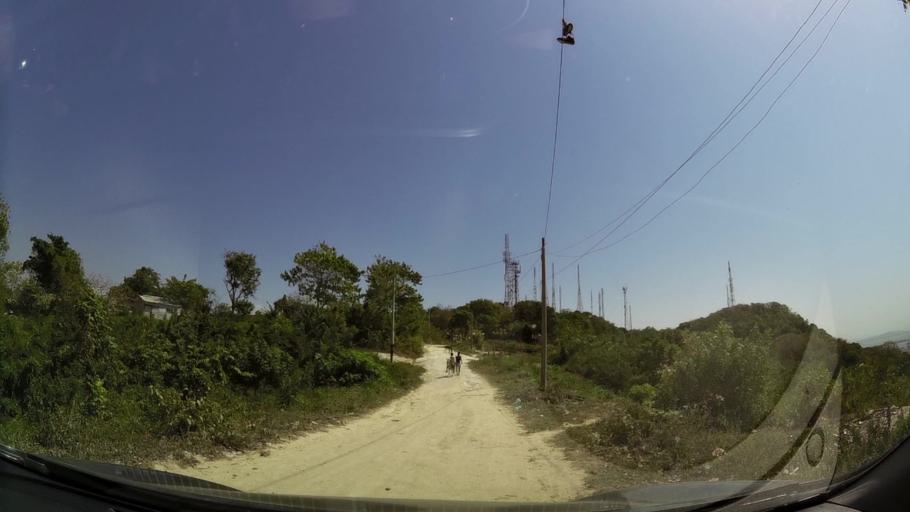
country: CO
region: Bolivar
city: Cartagena
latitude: 10.4247
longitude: -75.5261
